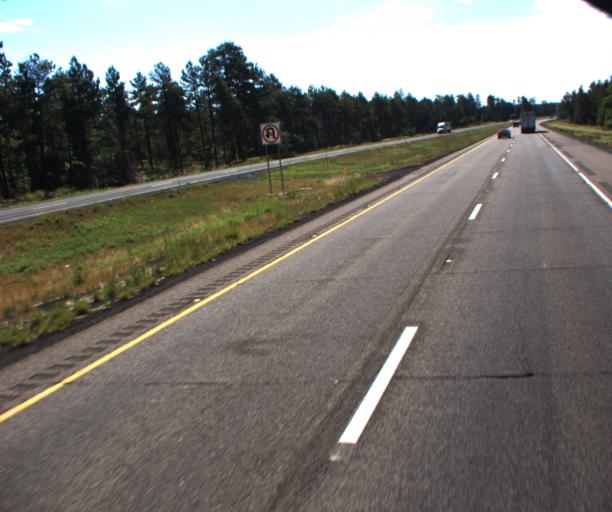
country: US
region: Arizona
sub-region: Coconino County
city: Sedona
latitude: 34.8594
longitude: -111.6136
